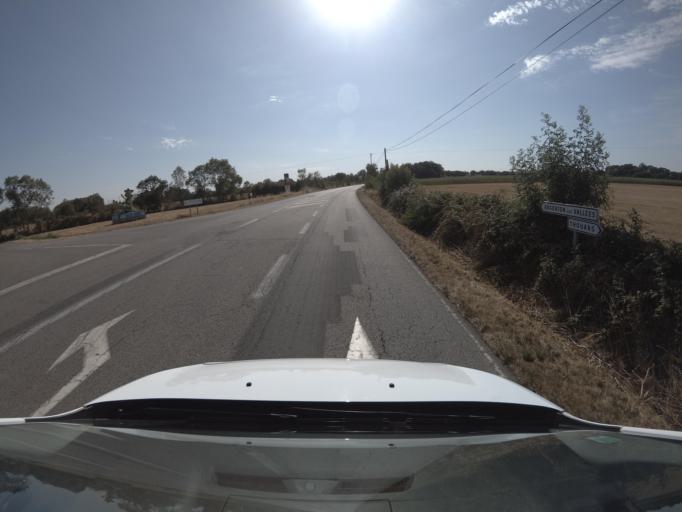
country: FR
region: Poitou-Charentes
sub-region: Departement des Deux-Sevres
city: Mauze-Thouarsais
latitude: 47.0041
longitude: -0.3537
